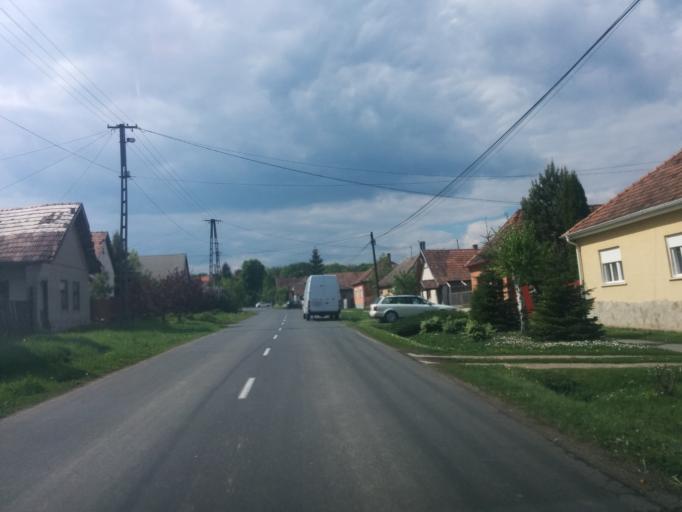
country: HU
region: Nograd
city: Romhany
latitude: 47.8445
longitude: 19.2968
